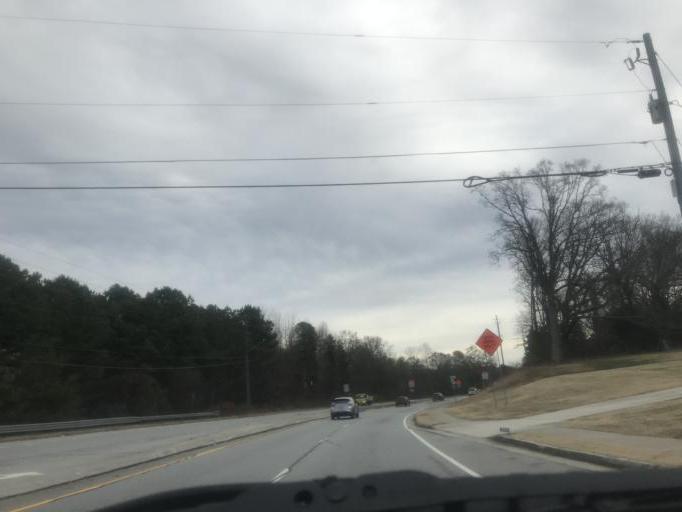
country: US
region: Georgia
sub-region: Gwinnett County
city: Buford
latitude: 34.0676
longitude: -83.9528
